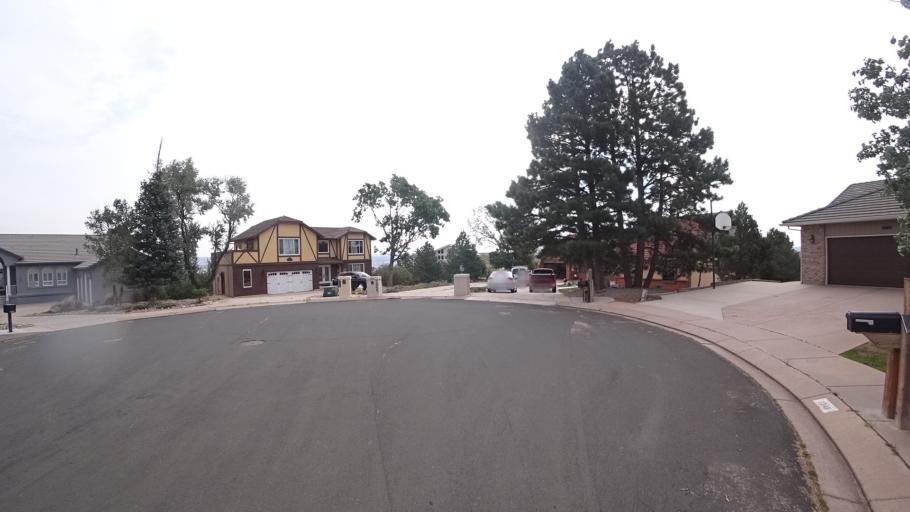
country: US
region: Colorado
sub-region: El Paso County
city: Air Force Academy
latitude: 38.9372
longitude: -104.8549
